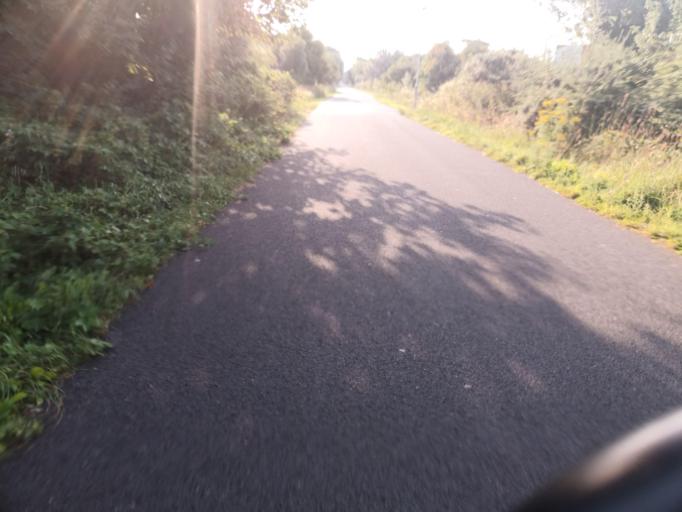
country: GB
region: Northern Ireland
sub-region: Castlereagh District
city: Dundonald
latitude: 54.5904
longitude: -5.8253
